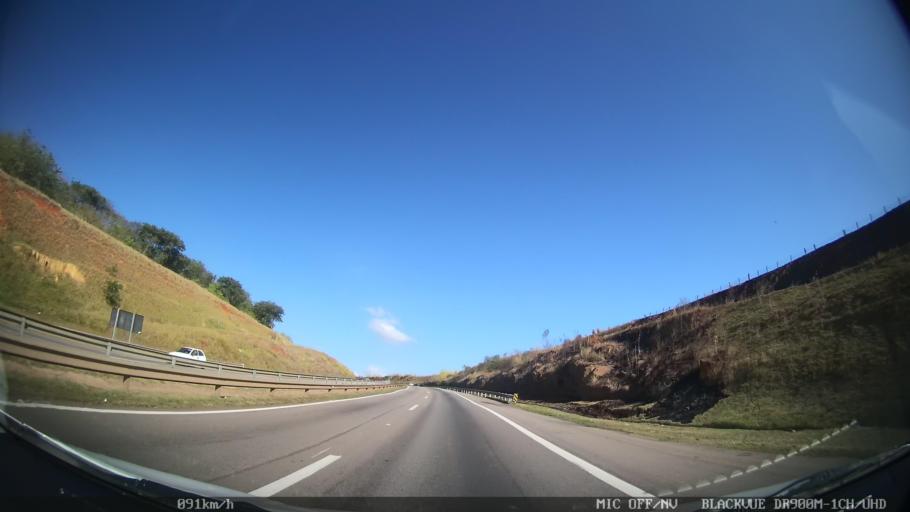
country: BR
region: Sao Paulo
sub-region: Piracicaba
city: Piracicaba
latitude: -22.7076
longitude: -47.6118
